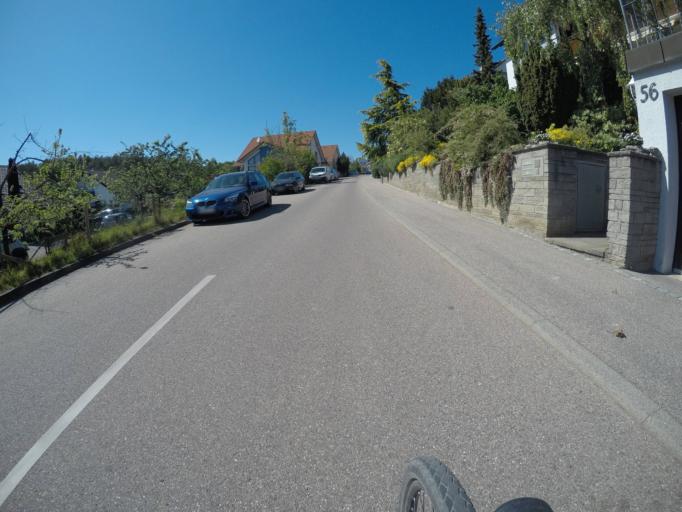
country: DE
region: Baden-Wuerttemberg
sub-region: Regierungsbezirk Stuttgart
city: Weissach
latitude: 48.8322
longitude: 8.9040
